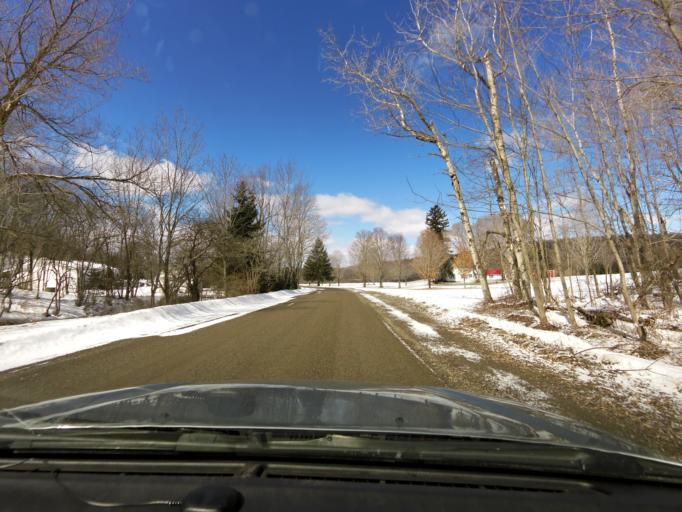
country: US
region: New York
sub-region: Cattaraugus County
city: Franklinville
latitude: 42.3433
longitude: -78.4240
